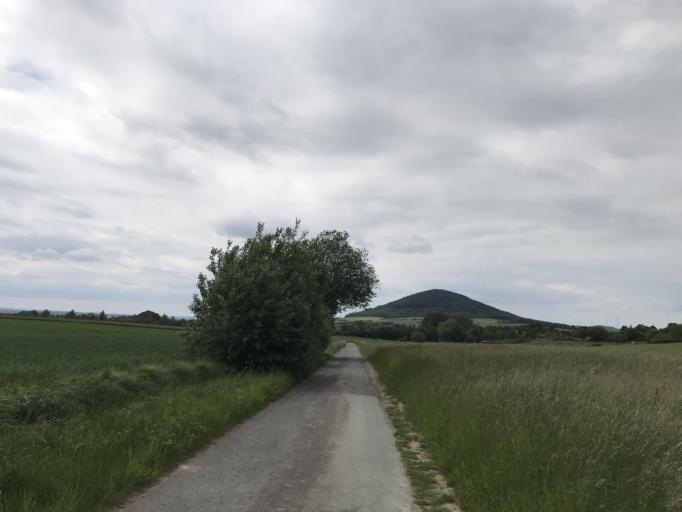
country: DE
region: Hesse
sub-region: Regierungsbezirk Kassel
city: Martinhagen
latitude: 51.2984
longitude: 9.2475
